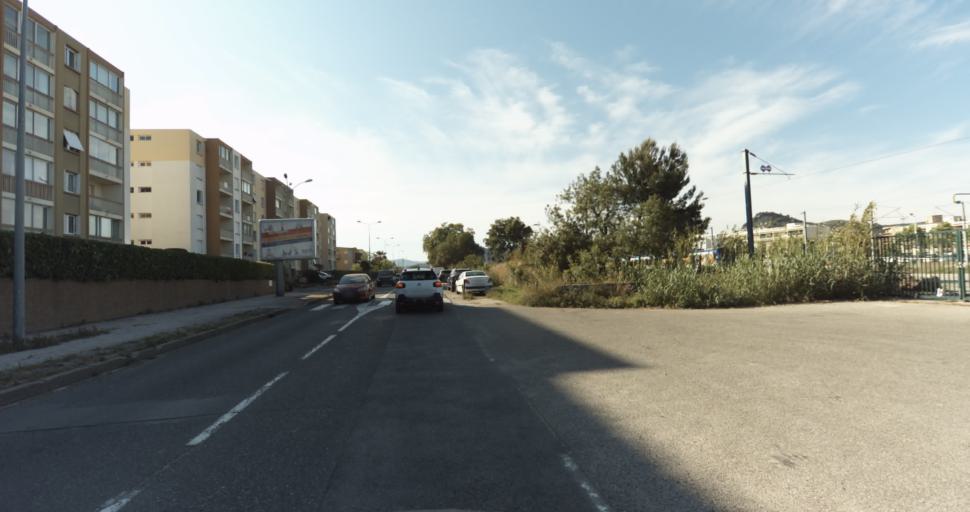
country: FR
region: Provence-Alpes-Cote d'Azur
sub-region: Departement du Var
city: Hyeres
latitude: 43.1072
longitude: 6.1253
